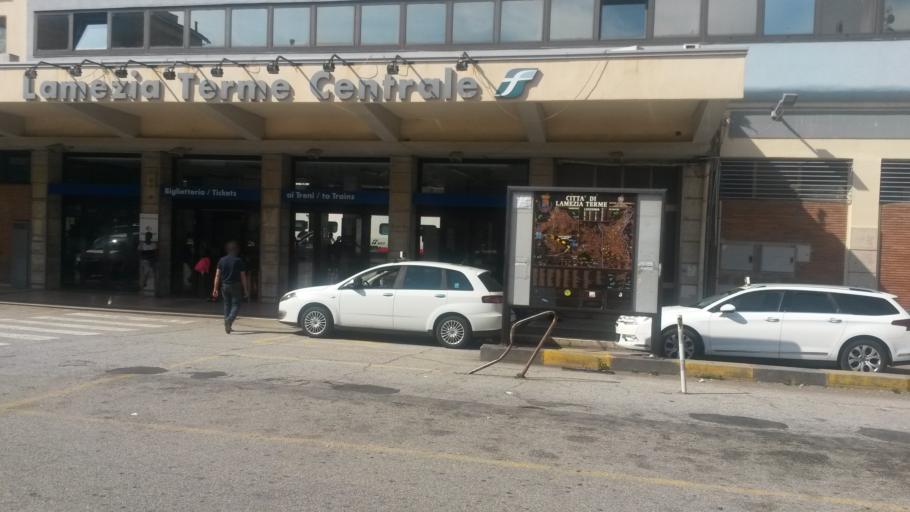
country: IT
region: Calabria
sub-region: Provincia di Catanzaro
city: Santa Eufemia Lamezia
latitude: 38.9210
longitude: 16.2554
